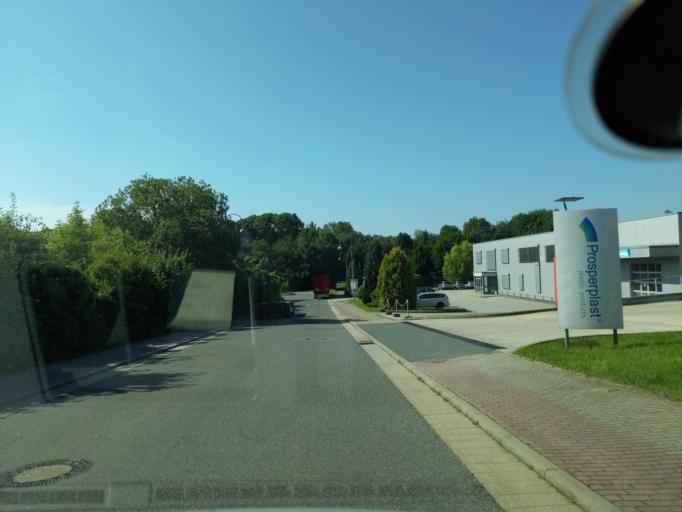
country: DE
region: Saxony
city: Lobau
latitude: 51.1065
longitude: 14.6578
